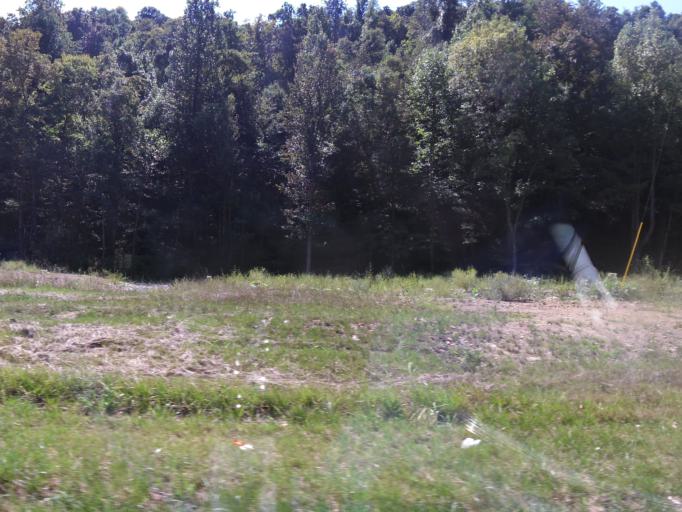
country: US
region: Kentucky
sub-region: Leslie County
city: Hyden
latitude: 37.0643
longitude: -83.4053
